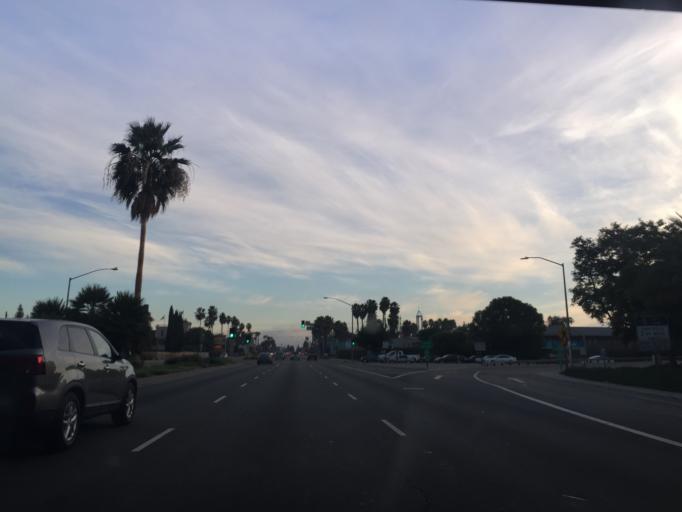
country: US
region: California
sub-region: Orange County
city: Buena Park
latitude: 33.8559
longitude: -117.9981
